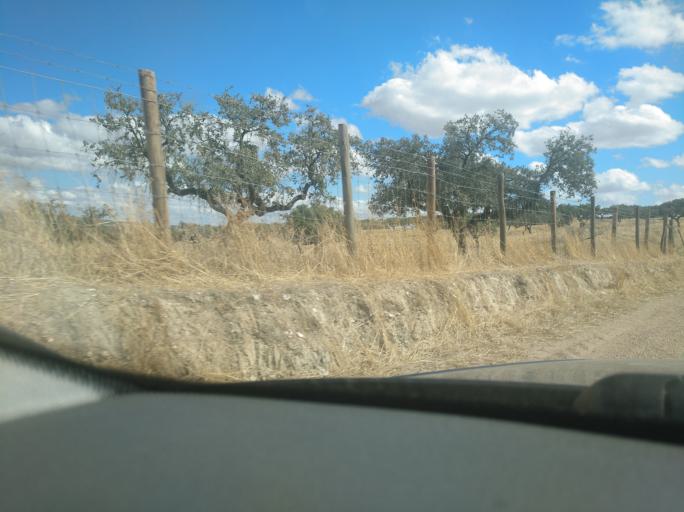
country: ES
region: Extremadura
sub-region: Provincia de Badajoz
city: La Codosera
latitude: 39.1338
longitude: -7.1563
